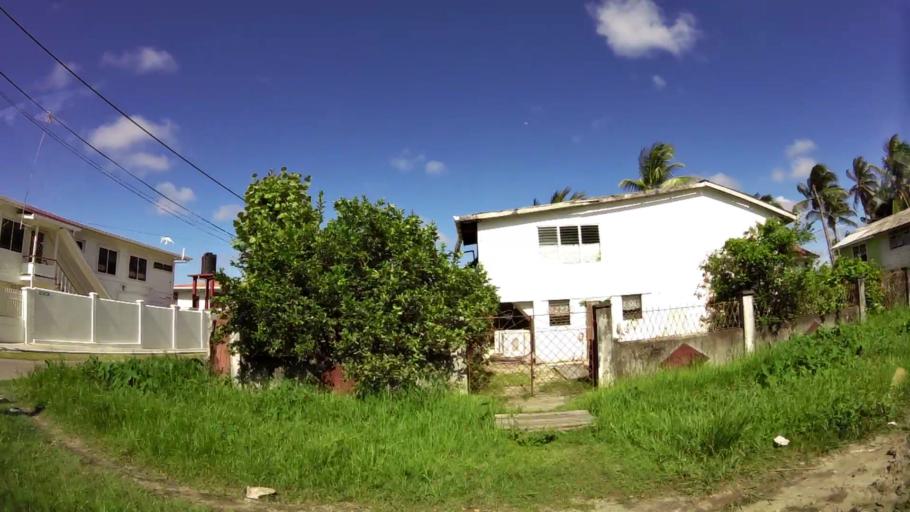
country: GY
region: Demerara-Mahaica
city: Georgetown
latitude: 6.8178
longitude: -58.1334
